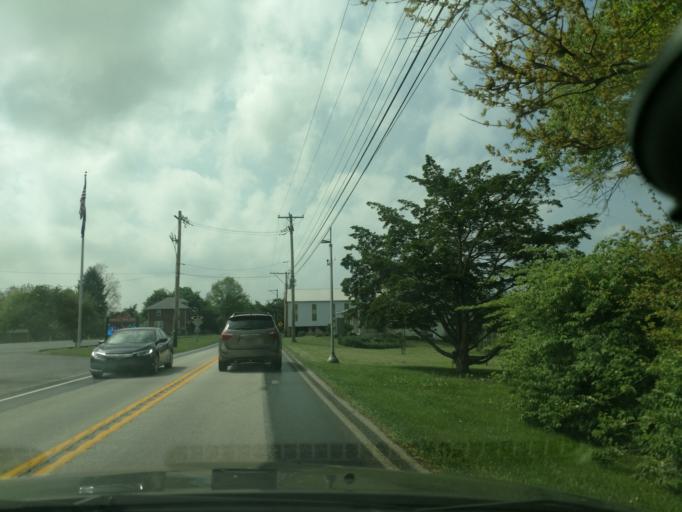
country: US
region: Pennsylvania
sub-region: Chester County
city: Kenilworth
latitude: 40.1742
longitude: -75.6161
